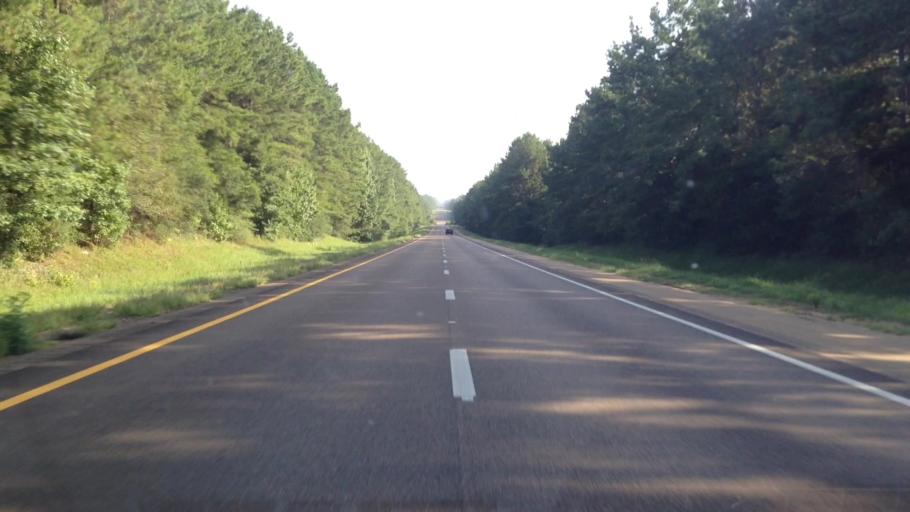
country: US
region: Mississippi
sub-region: Pike County
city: Summit
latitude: 31.3724
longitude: -90.4792
